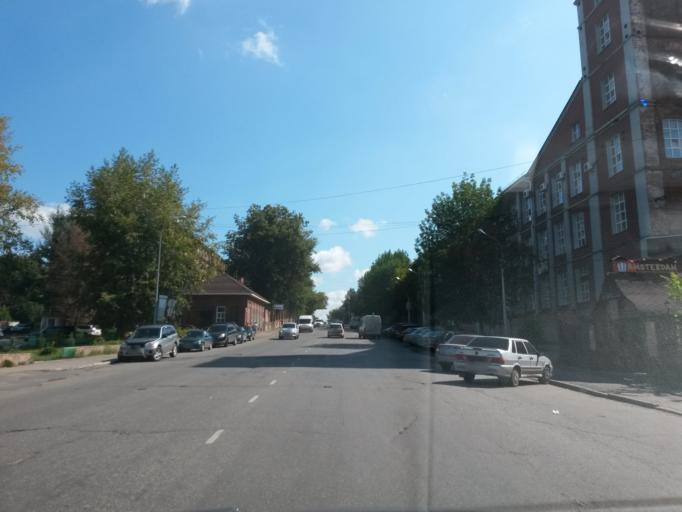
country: RU
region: Ivanovo
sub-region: Gorod Ivanovo
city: Ivanovo
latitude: 57.0103
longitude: 40.9664
